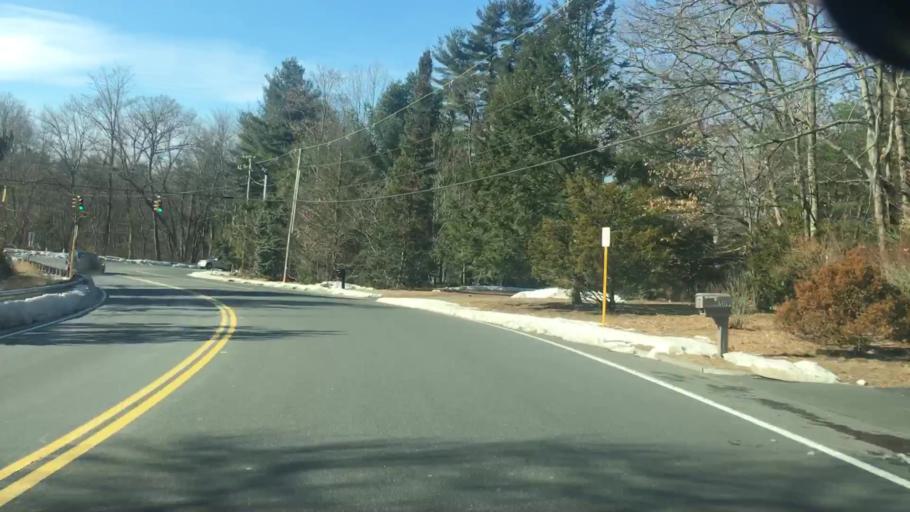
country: US
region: Massachusetts
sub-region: Hampden County
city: East Longmeadow
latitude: 42.0571
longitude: -72.5343
